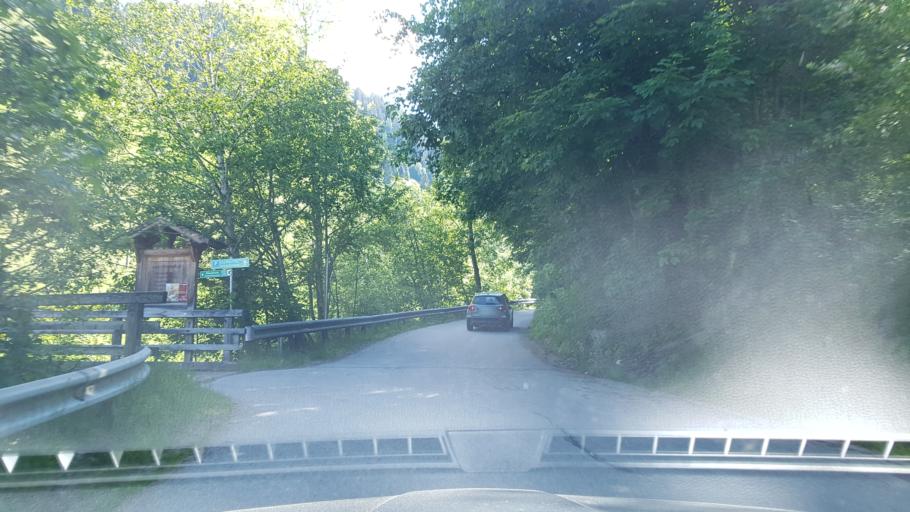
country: AT
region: Salzburg
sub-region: Politischer Bezirk Sankt Johann im Pongau
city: Huttschlag
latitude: 47.2346
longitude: 13.2540
